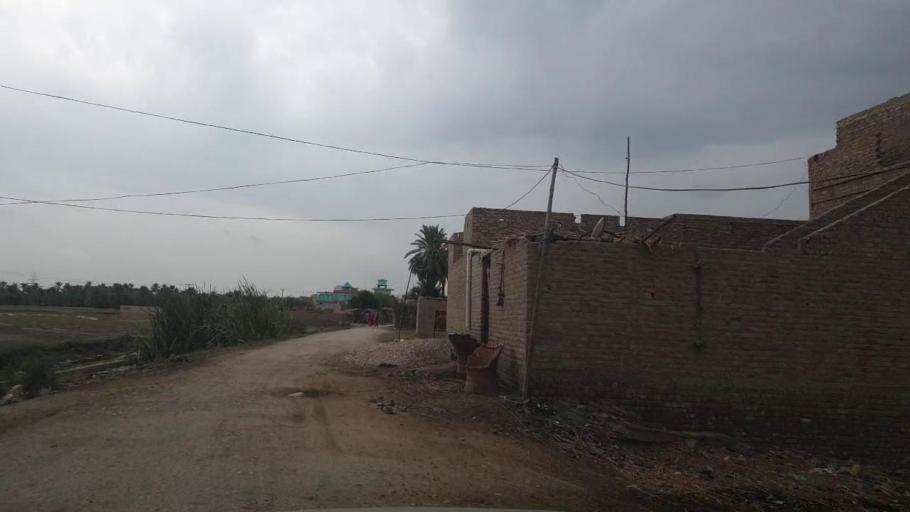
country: PK
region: Sindh
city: Khairpur
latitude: 27.5411
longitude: 68.7366
